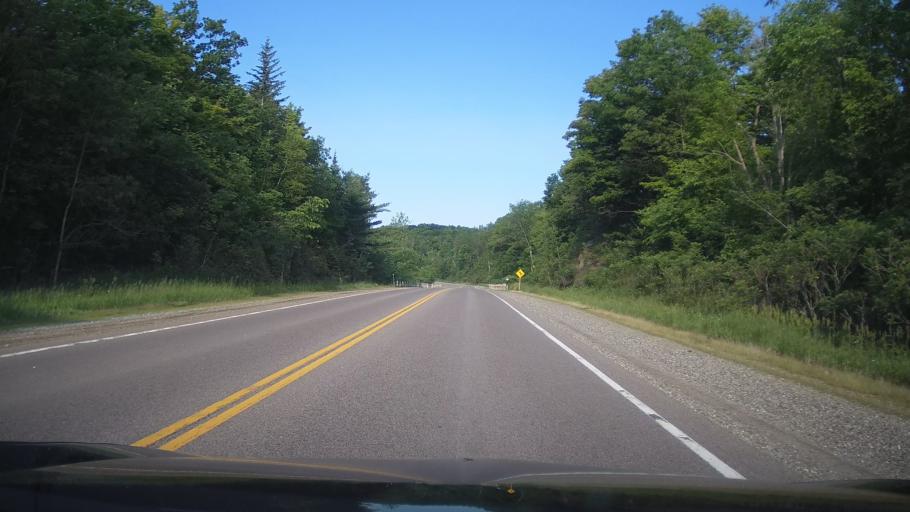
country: CA
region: Ontario
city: Perth
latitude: 44.7851
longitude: -76.7164
